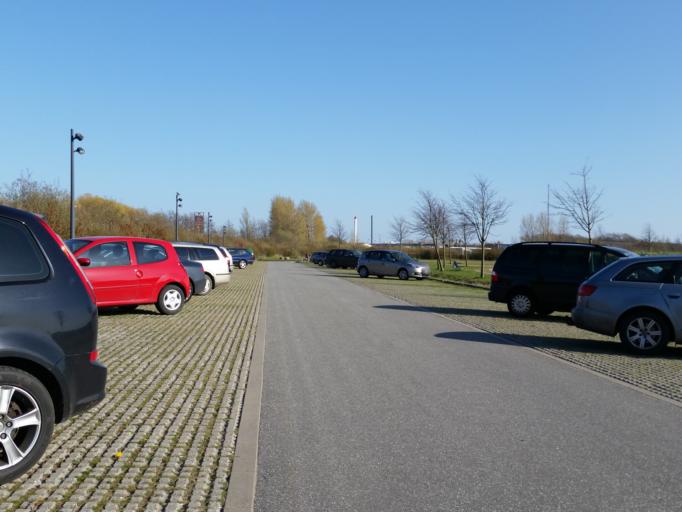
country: DK
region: South Denmark
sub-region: Nyborg Kommune
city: Nyborg
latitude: 55.3124
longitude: 10.8028
